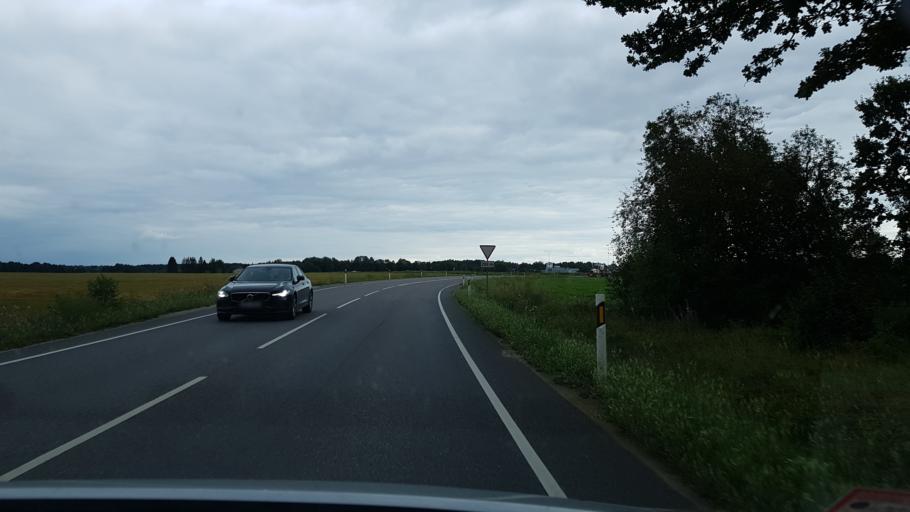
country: EE
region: Tartu
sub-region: Tartu linn
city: Tartu
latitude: 58.3701
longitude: 26.8841
